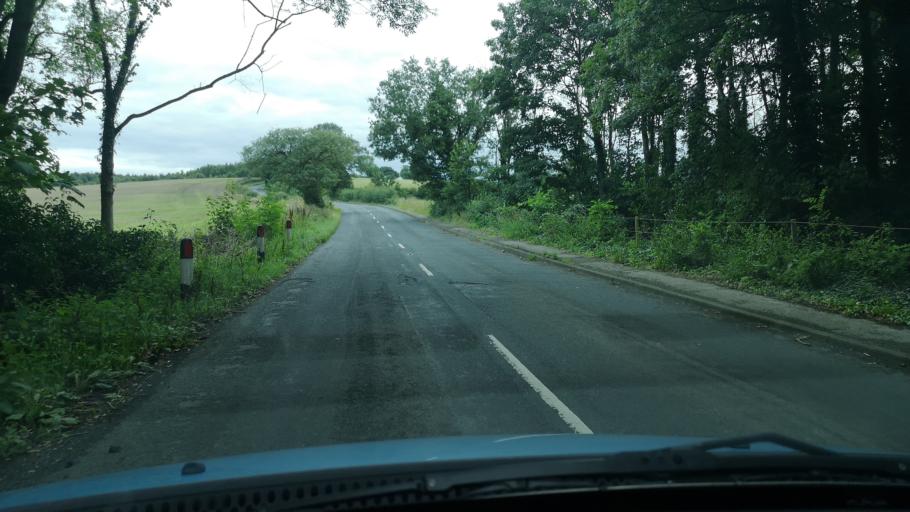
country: GB
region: England
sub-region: City and Borough of Wakefield
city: Crigglestone
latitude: 53.6290
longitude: -1.5529
